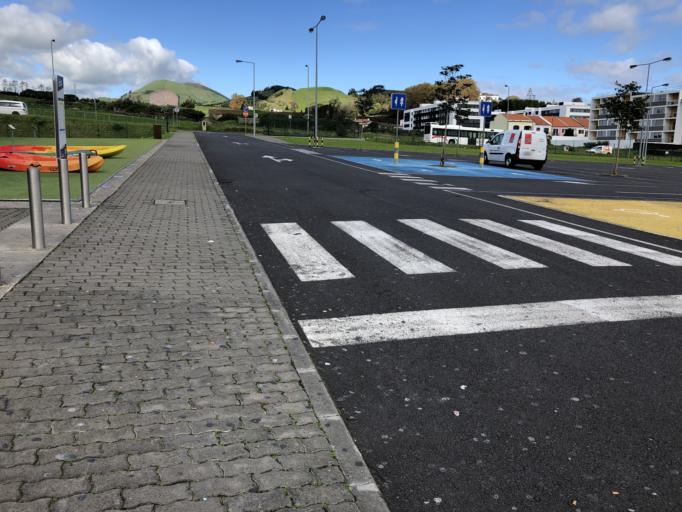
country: PT
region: Azores
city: Ponta Delgada
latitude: 37.7534
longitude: -25.6716
